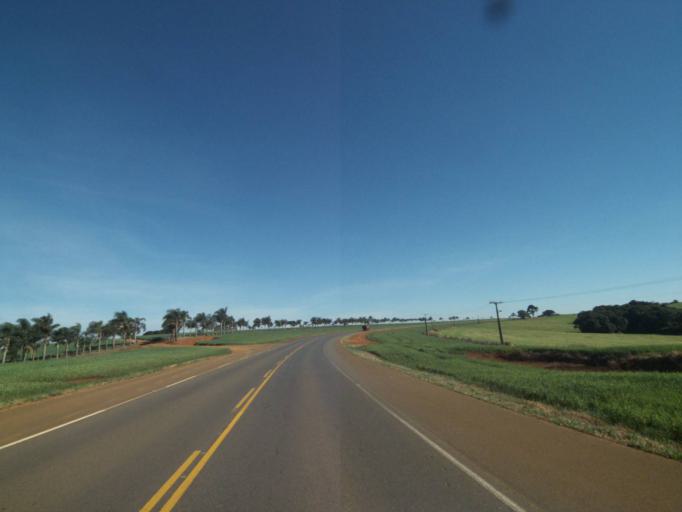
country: BR
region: Parana
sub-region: Tibagi
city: Tibagi
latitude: -24.4218
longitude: -50.3730
